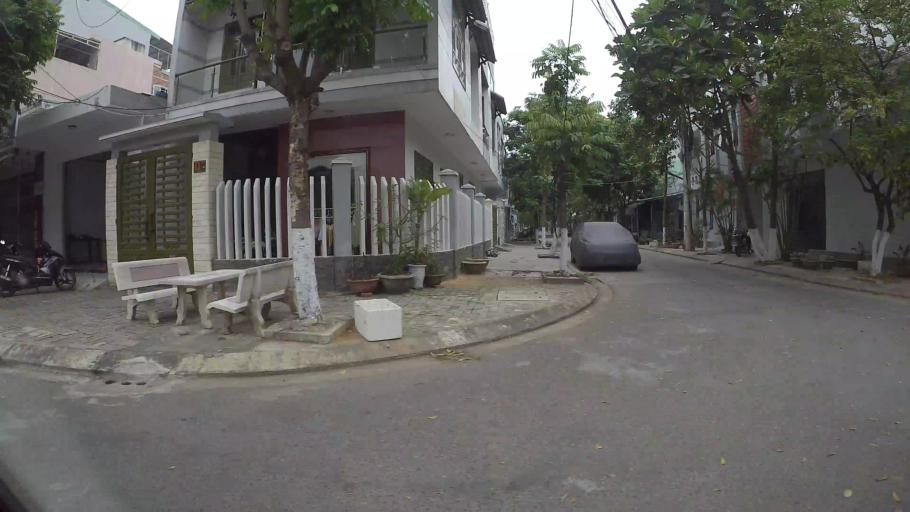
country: VN
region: Da Nang
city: Cam Le
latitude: 16.0275
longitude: 108.2133
